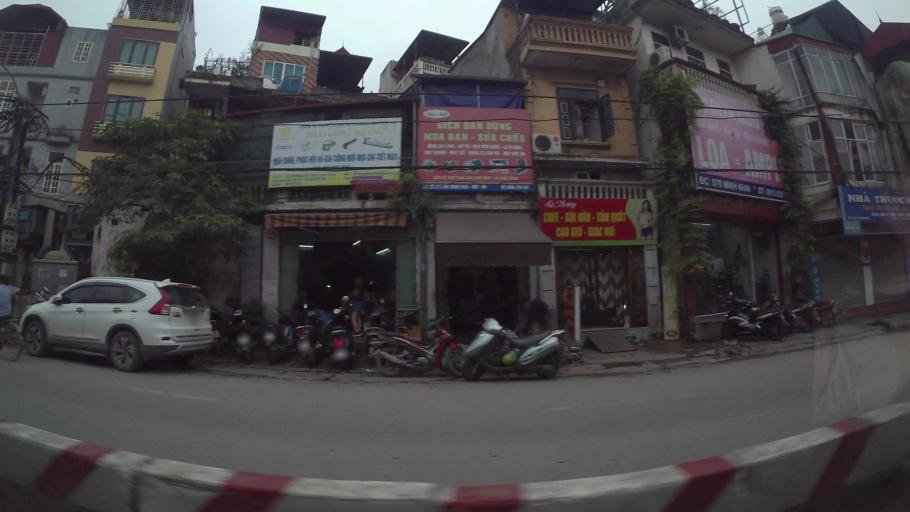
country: VN
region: Ha Noi
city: Hai BaTrung
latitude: 21.0040
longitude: 105.8693
